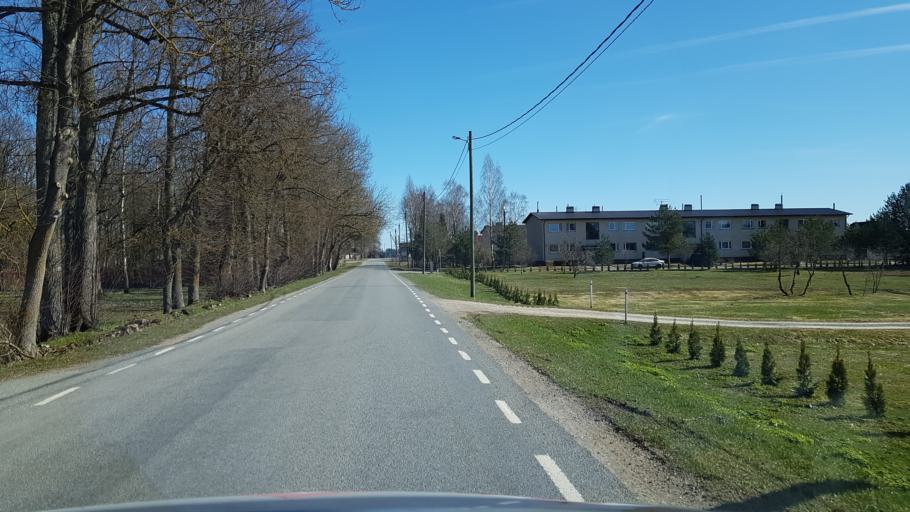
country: EE
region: Laeaene-Virumaa
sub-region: Someru vald
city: Someru
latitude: 59.3426
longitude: 26.5086
